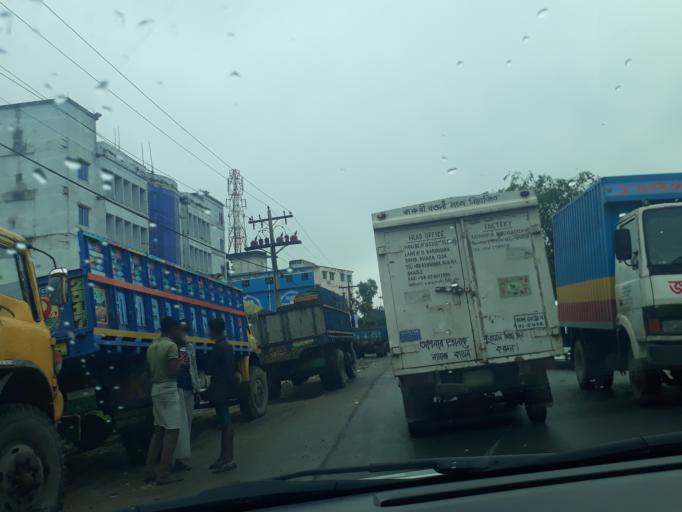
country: BD
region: Dhaka
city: Tungi
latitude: 23.9064
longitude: 90.3221
